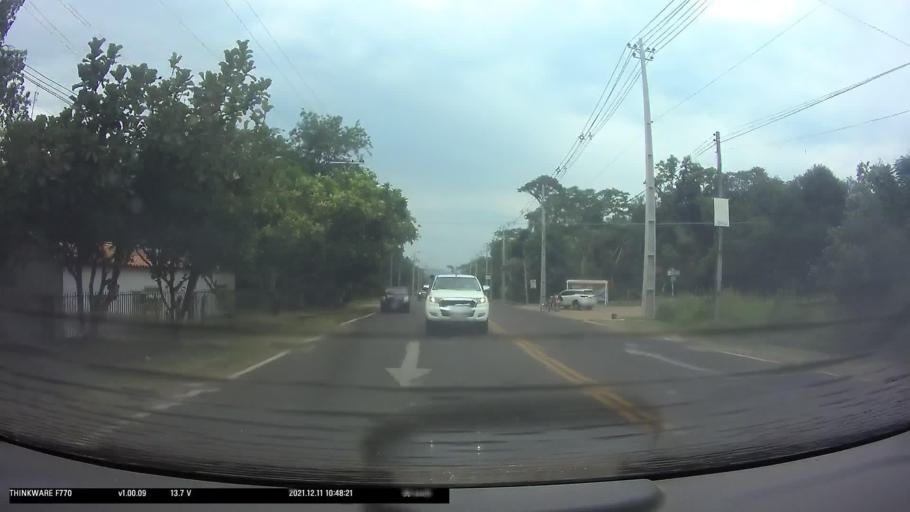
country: PY
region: Cordillera
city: San Bernardino
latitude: -25.3003
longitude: -57.2884
